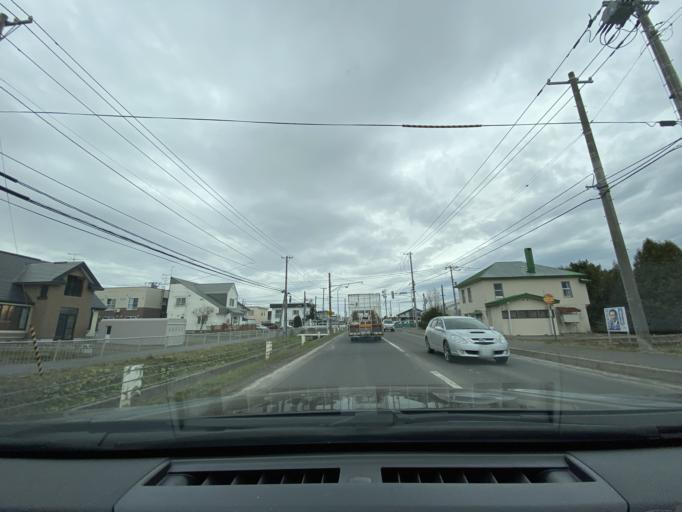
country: JP
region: Hokkaido
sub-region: Asahikawa-shi
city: Asahikawa
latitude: 43.7853
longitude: 142.4174
